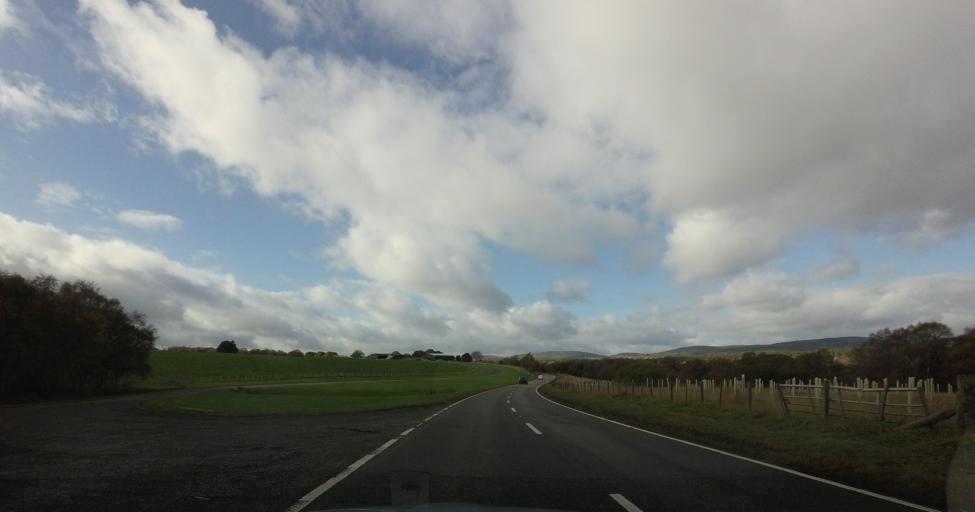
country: GB
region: Scotland
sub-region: Highland
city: Grantown on Spey
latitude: 57.3207
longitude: -3.5631
